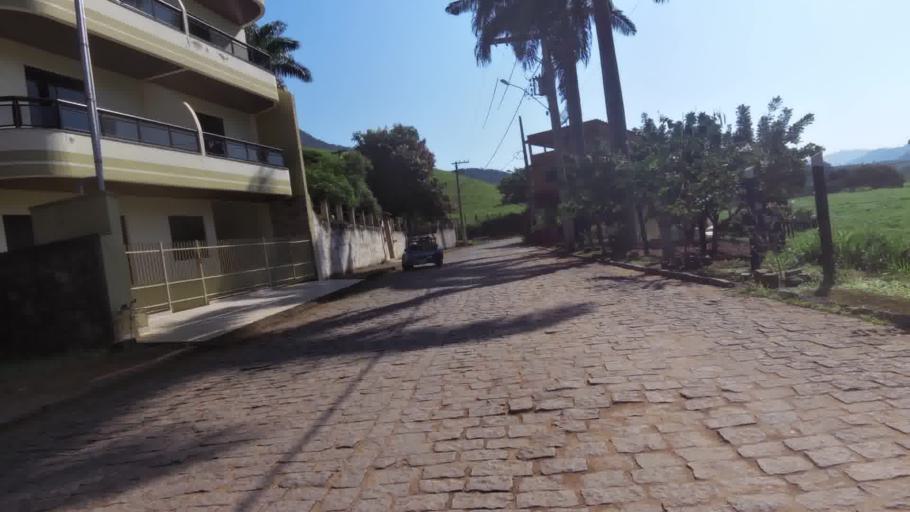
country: BR
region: Espirito Santo
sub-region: Alfredo Chaves
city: Alfredo Chaves
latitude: -20.6788
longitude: -40.7720
